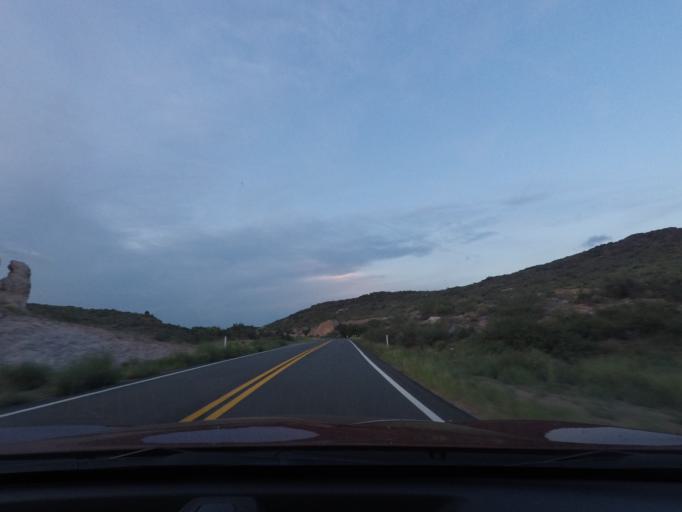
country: US
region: Arizona
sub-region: Yavapai County
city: Prescott
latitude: 34.4417
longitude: -112.6946
